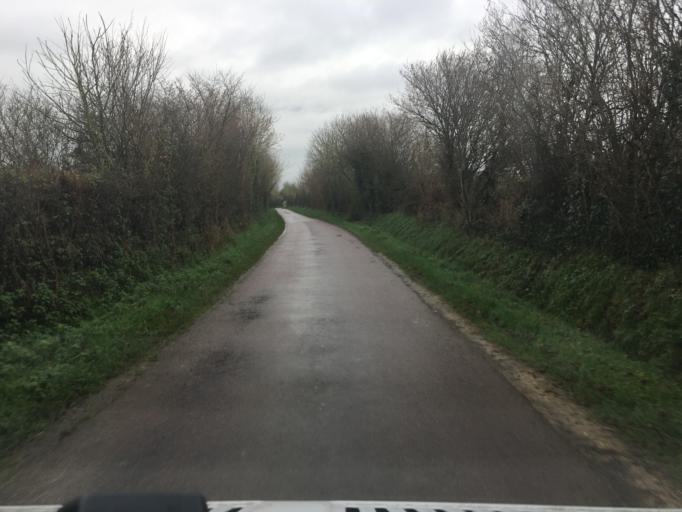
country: FR
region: Lower Normandy
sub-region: Departement de la Manche
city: Sainte-Mere-Eglise
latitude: 49.4236
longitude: -1.2690
